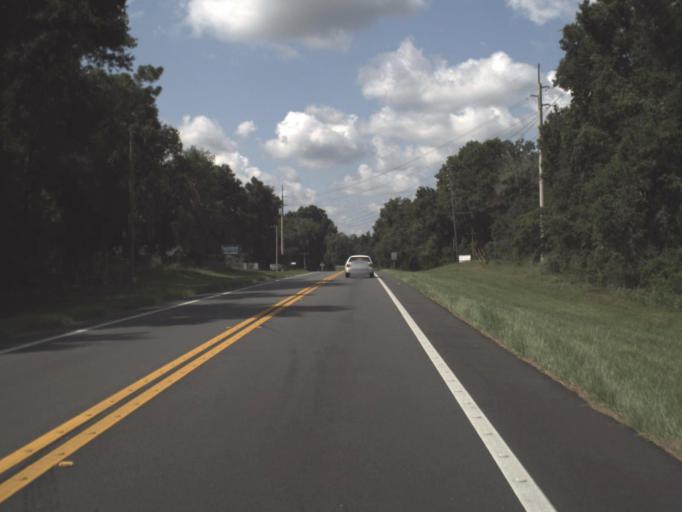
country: US
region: Florida
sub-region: Citrus County
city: Floral City
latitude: 28.7304
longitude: -82.3043
